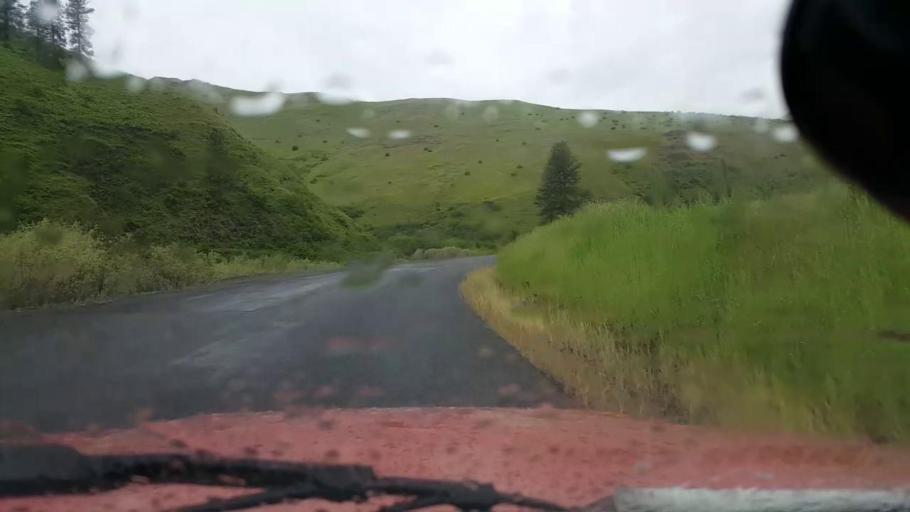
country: US
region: Washington
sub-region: Asotin County
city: Asotin
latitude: 46.0277
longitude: -117.3112
